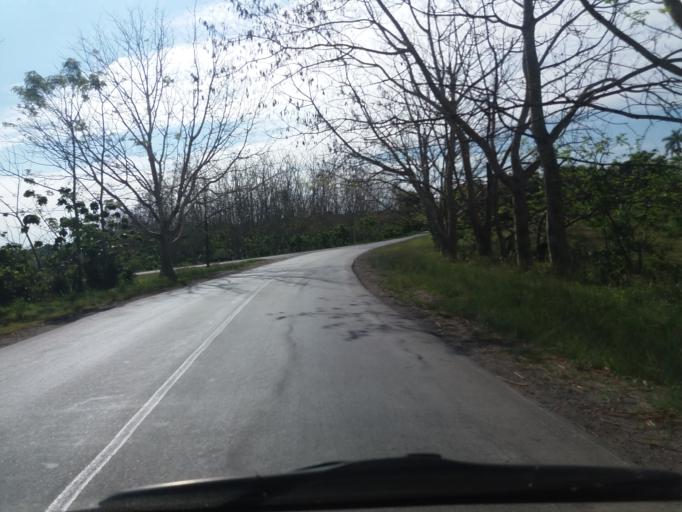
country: CU
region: Cienfuegos
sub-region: Municipio de Cienfuegos
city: Cienfuegos
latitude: 22.1653
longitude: -80.3698
